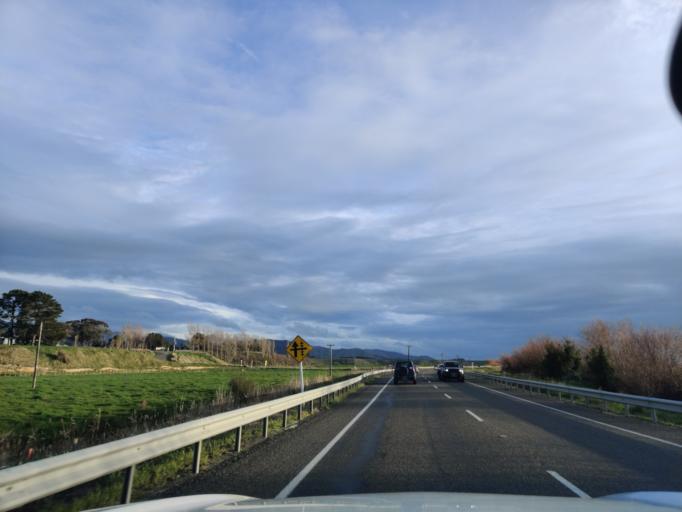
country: NZ
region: Manawatu-Wanganui
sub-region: Horowhenua District
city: Foxton
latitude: -40.5256
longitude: 175.4431
